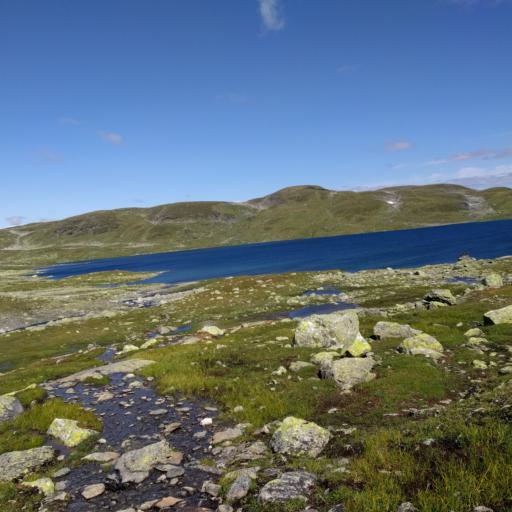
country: NO
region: Aust-Agder
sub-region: Bykle
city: Hovden
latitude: 59.8679
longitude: 7.2159
